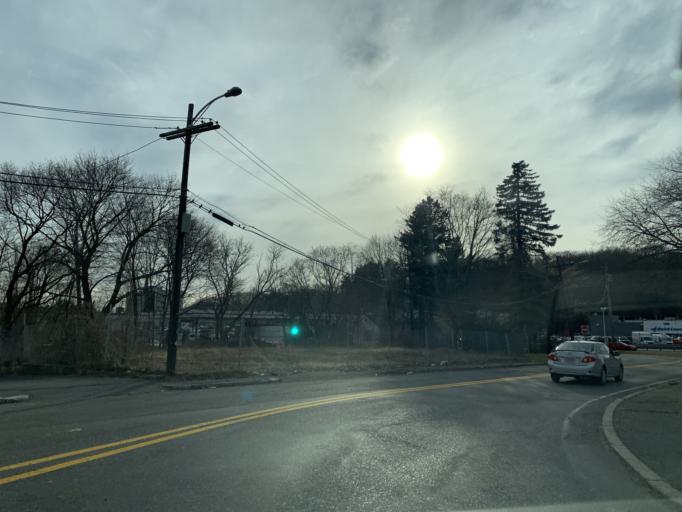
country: US
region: Massachusetts
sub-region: Essex County
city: Saugus
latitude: 42.4567
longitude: -71.0226
